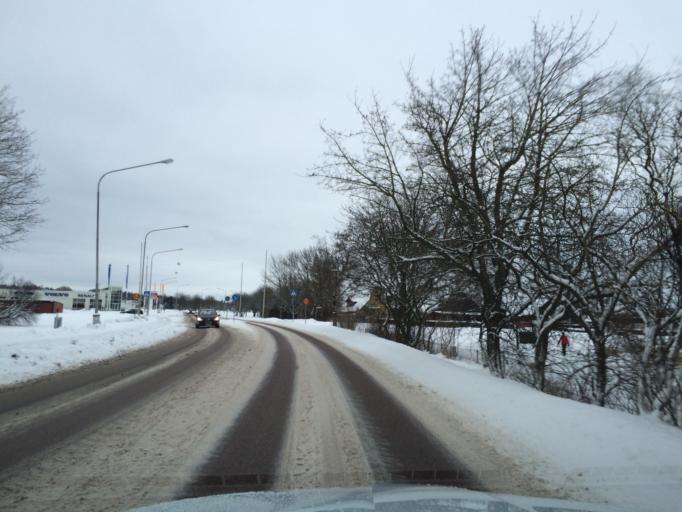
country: SE
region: Vaestmanland
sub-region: Hallstahammars Kommun
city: Hallstahammar
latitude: 59.6099
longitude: 16.2398
